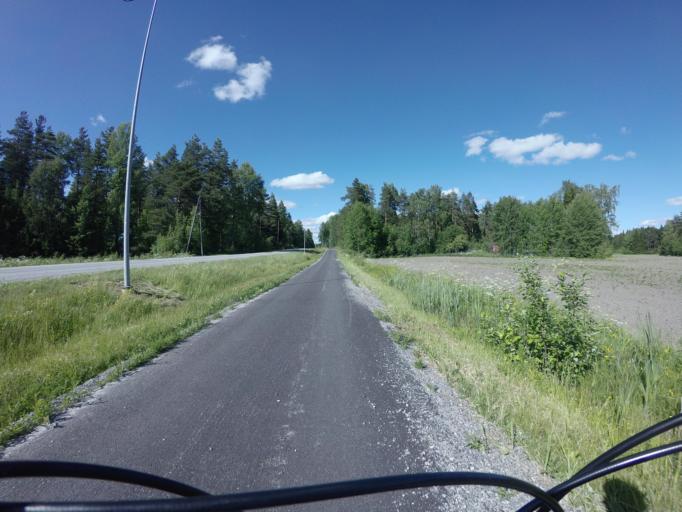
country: FI
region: Varsinais-Suomi
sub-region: Turku
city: Turku
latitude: 60.5193
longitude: 22.2936
